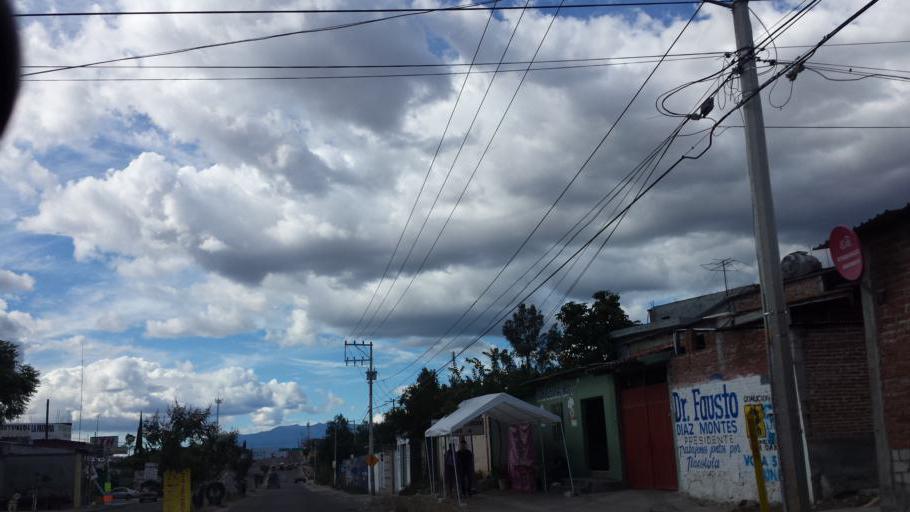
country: MX
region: Oaxaca
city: Tlacolula de Matamoros
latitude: 16.9545
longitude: -96.4701
